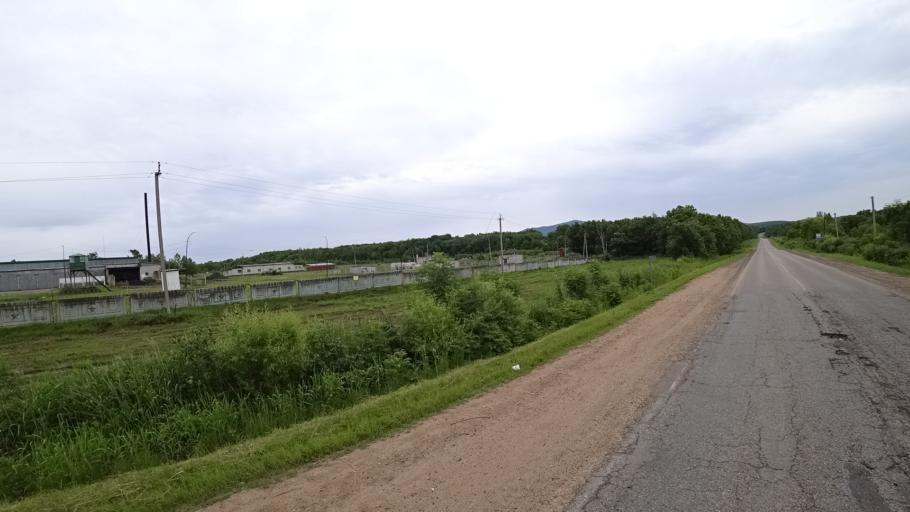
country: RU
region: Primorskiy
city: Novosysoyevka
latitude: 44.1795
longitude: 133.3484
